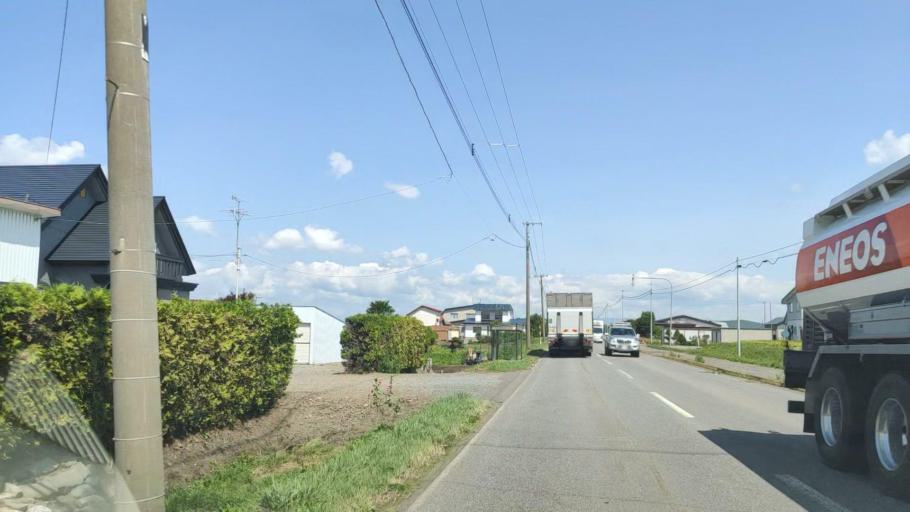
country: JP
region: Hokkaido
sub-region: Asahikawa-shi
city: Asahikawa
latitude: 43.7202
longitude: 142.4578
